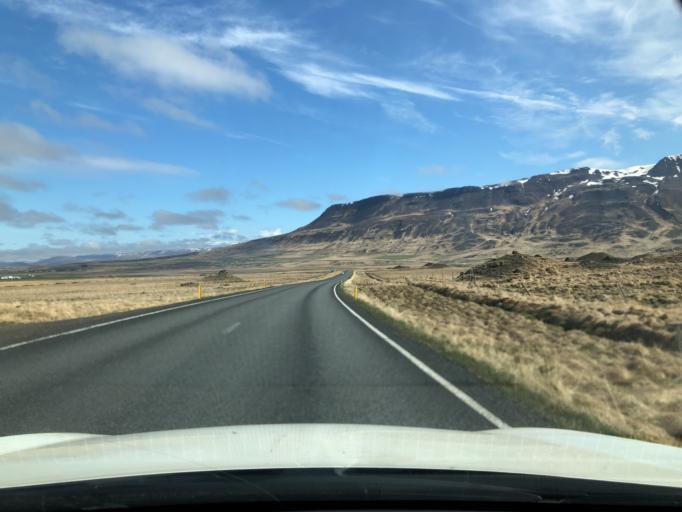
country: IS
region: Northwest
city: Saudarkrokur
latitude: 65.5005
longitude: -20.3993
